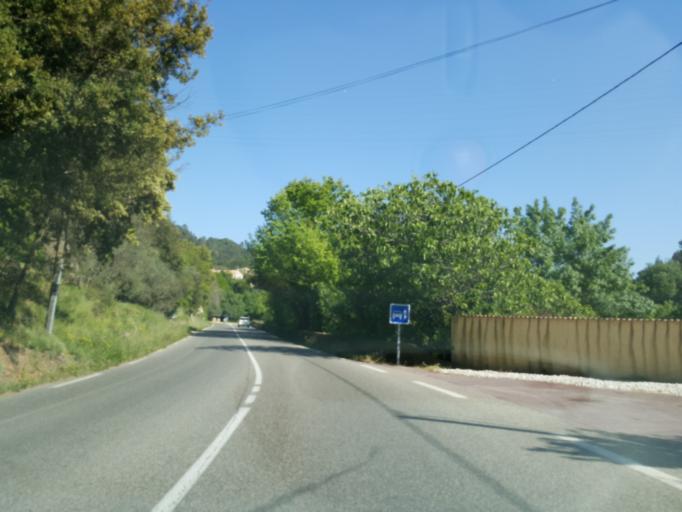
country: FR
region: Provence-Alpes-Cote d'Azur
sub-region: Departement du Var
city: Belgentier
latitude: 43.2548
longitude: 5.9891
